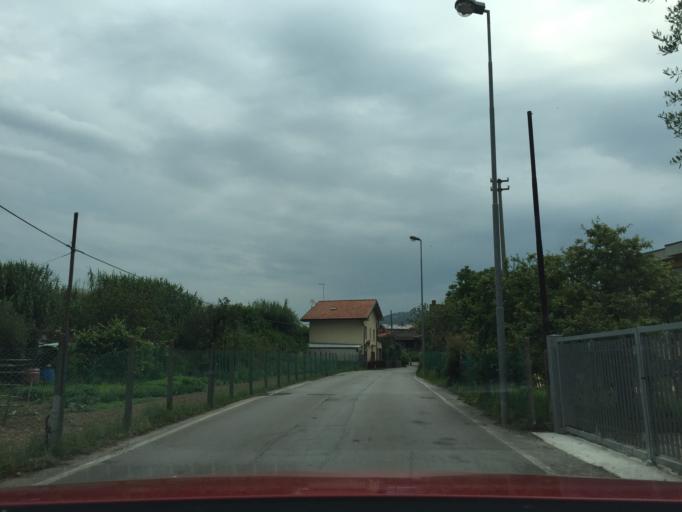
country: IT
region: Tuscany
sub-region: Provincia di Pistoia
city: Pieve a Nievole
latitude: 43.8802
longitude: 10.8093
